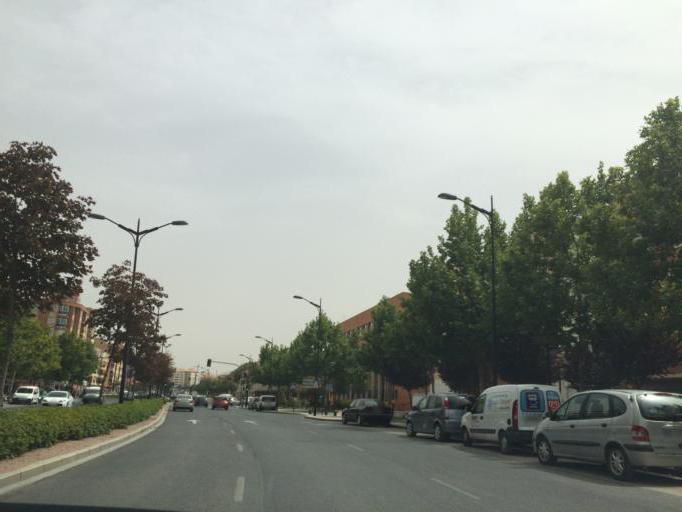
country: ES
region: Castille-La Mancha
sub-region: Provincia de Albacete
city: Albacete
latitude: 38.9855
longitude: -1.8650
